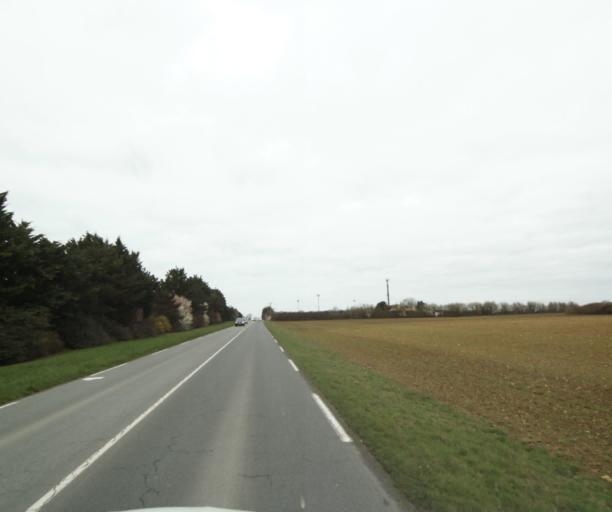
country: FR
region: Poitou-Charentes
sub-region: Departement de la Charente-Maritime
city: Lagord
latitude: 46.1938
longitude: -1.1507
